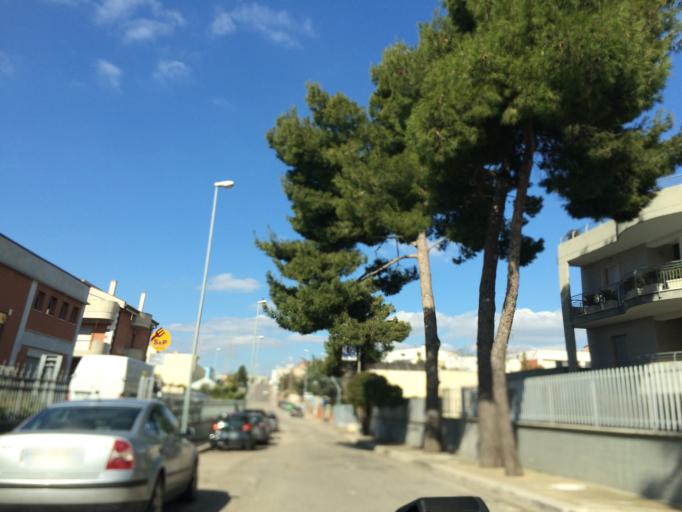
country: IT
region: Basilicate
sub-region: Provincia di Matera
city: Matera
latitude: 40.6703
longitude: 16.5769
